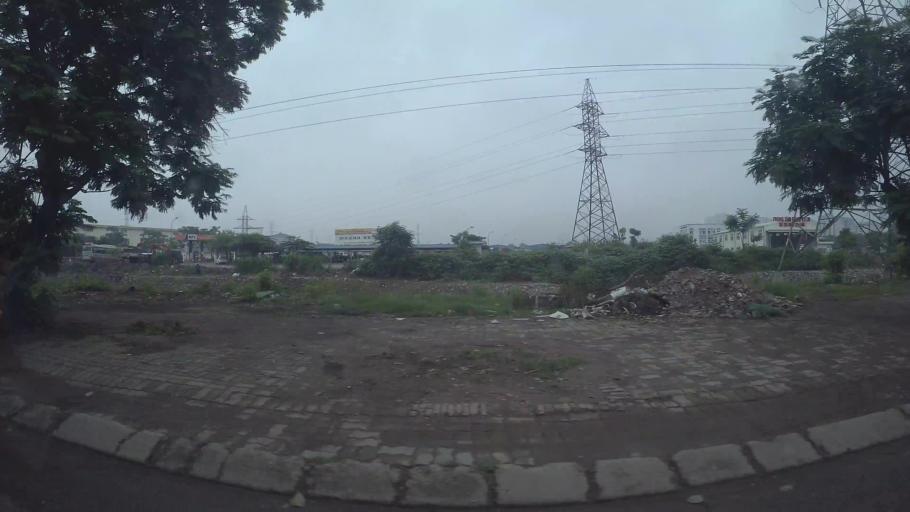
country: VN
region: Ha Noi
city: Hai BaTrung
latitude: 20.9801
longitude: 105.8646
